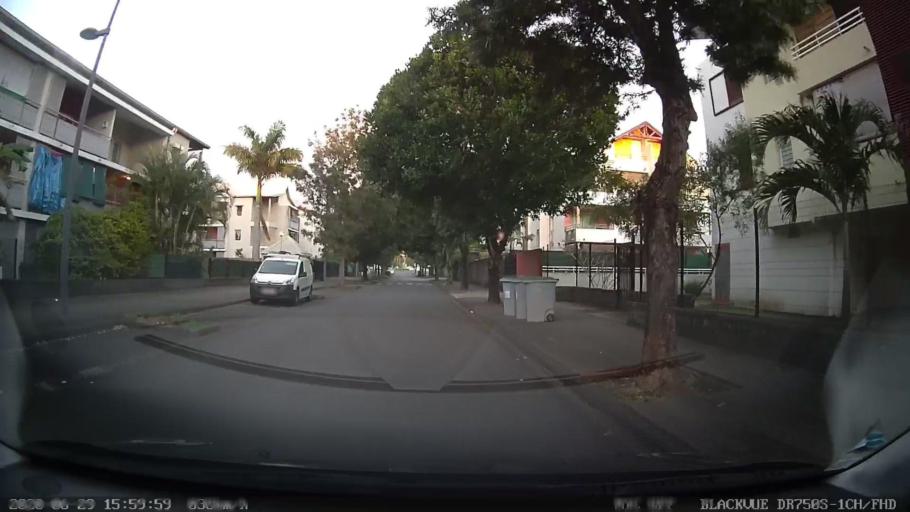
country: RE
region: Reunion
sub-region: Reunion
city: Bras-Panon
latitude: -21.0009
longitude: 55.6898
